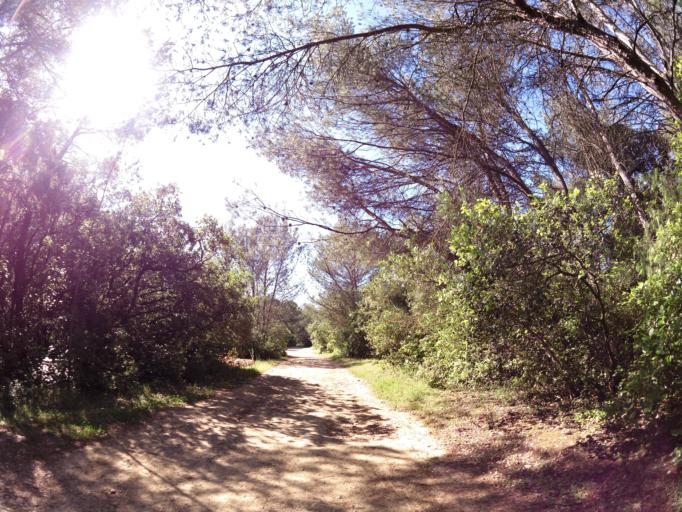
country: FR
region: Languedoc-Roussillon
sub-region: Departement du Gard
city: Mus
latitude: 43.7464
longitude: 4.1991
